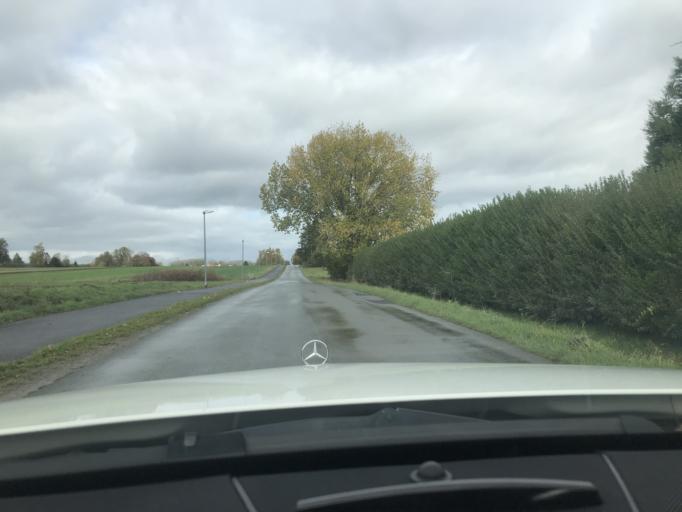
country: DE
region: Thuringia
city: Langula
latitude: 51.1553
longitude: 10.4210
